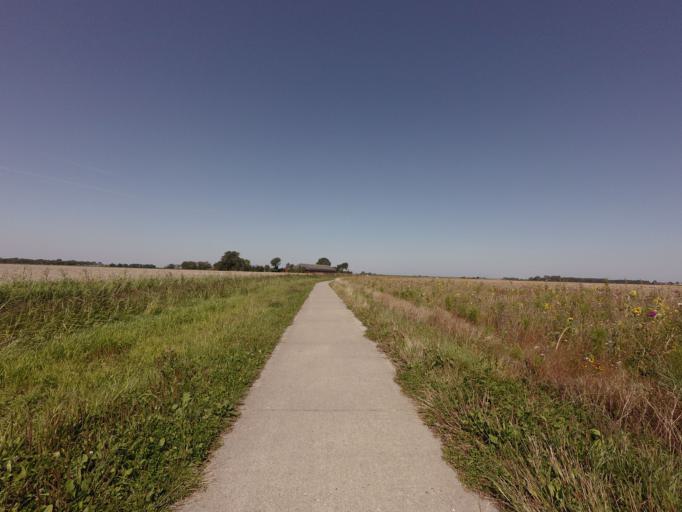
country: NL
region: Friesland
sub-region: Gemeente Dongeradeel
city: Anjum
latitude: 53.3892
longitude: 6.0661
